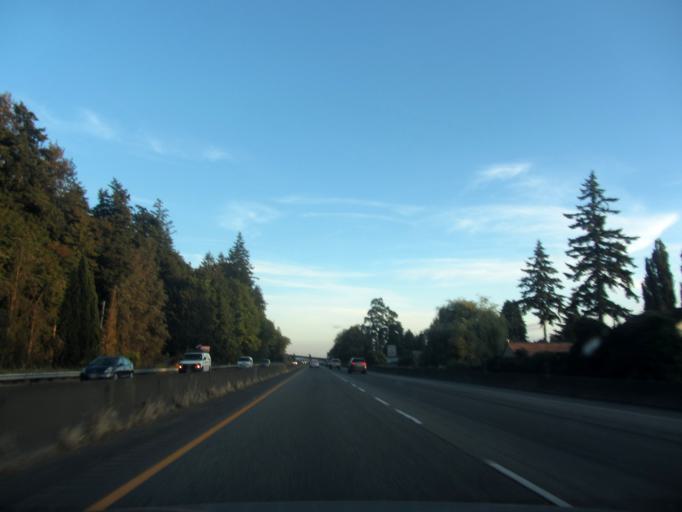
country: US
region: Washington
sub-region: Skagit County
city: Mount Vernon
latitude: 48.4117
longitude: -122.3315
